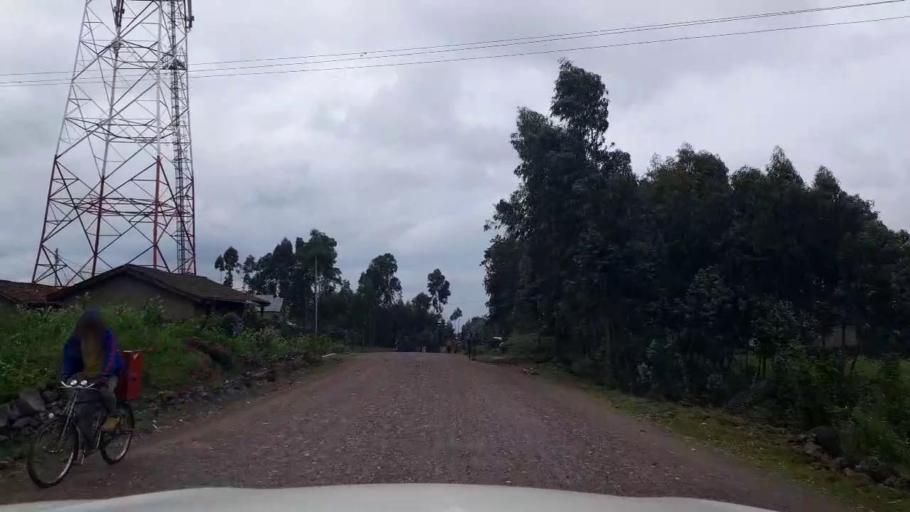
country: RW
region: Northern Province
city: Musanze
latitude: -1.5914
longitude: 29.4638
